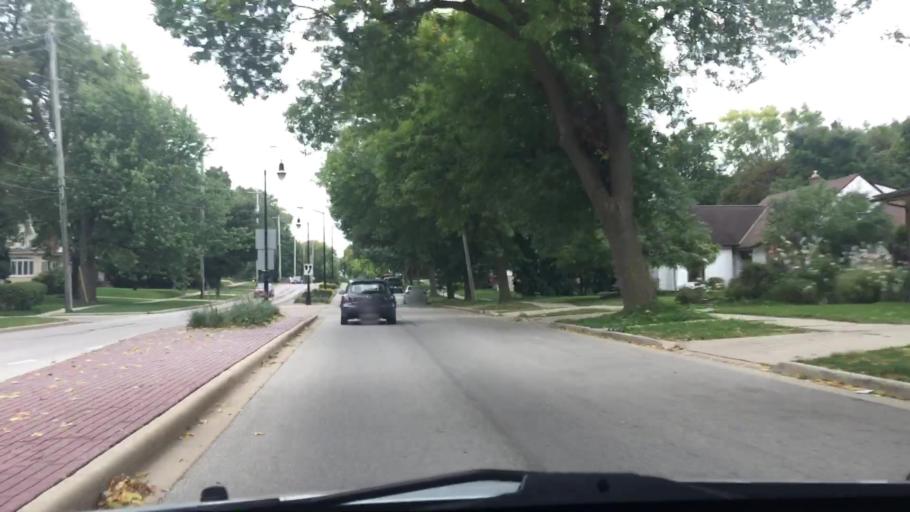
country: US
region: Wisconsin
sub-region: Waukesha County
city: Waukesha
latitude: 43.0025
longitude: -88.2319
